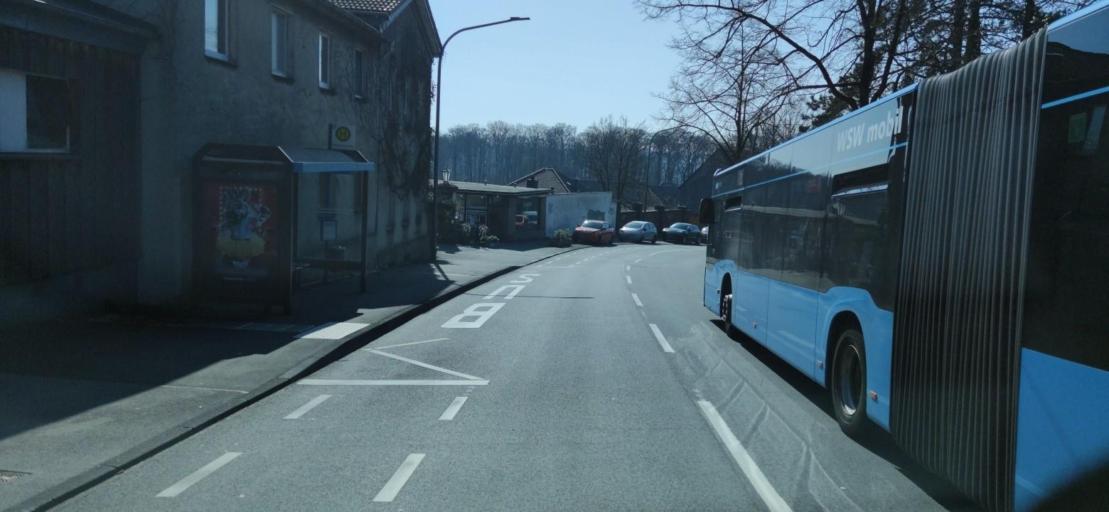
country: DE
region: North Rhine-Westphalia
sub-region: Regierungsbezirk Dusseldorf
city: Wuppertal
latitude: 51.2739
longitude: 7.1309
